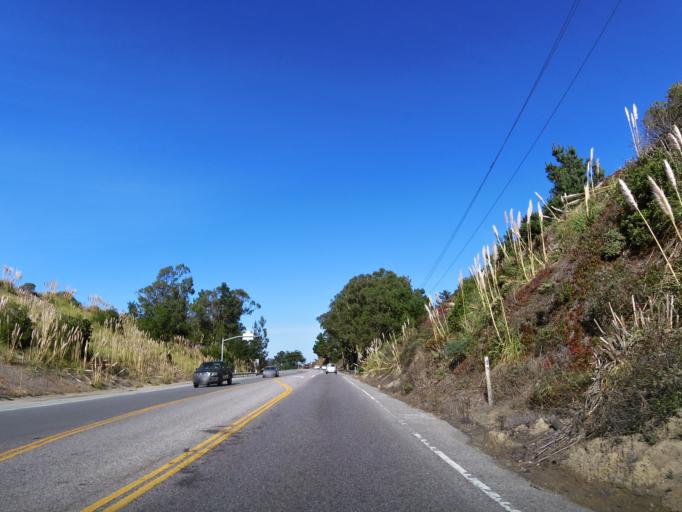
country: US
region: California
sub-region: San Mateo County
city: Colma
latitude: 37.6506
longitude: -122.4715
